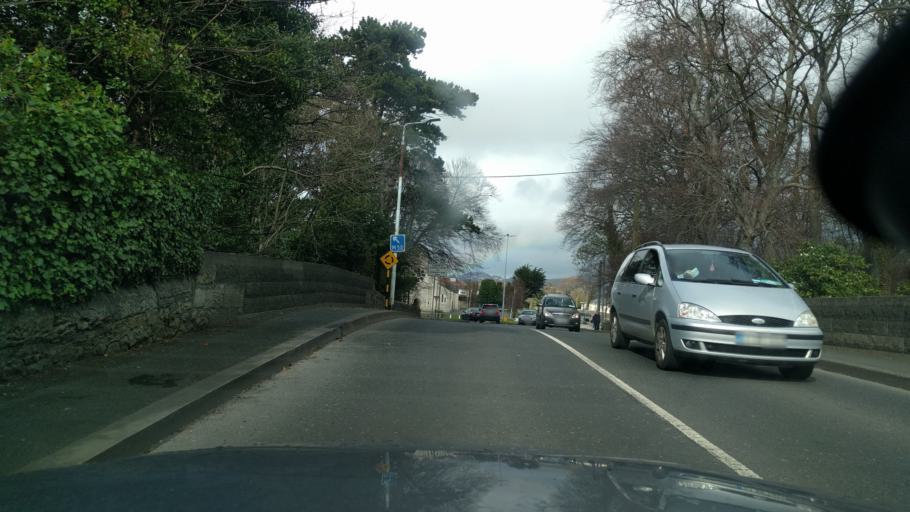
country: IE
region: Leinster
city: Shankill
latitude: 53.2323
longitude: -6.1239
